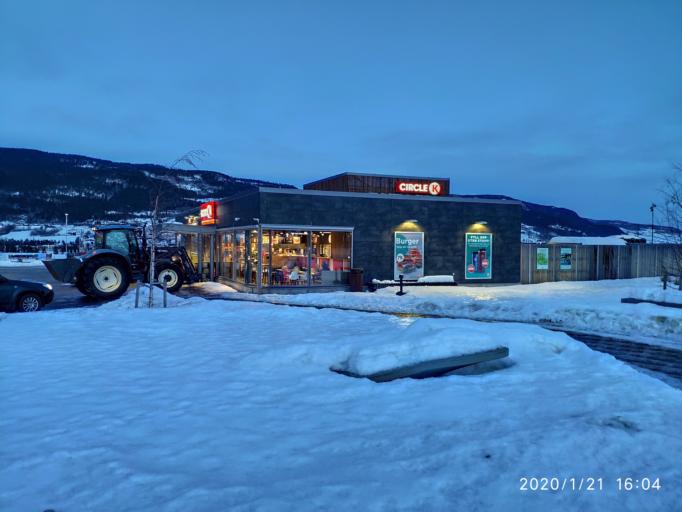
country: NO
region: Oppland
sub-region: Nord-Fron
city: Vinstra
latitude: 61.5917
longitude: 9.7223
